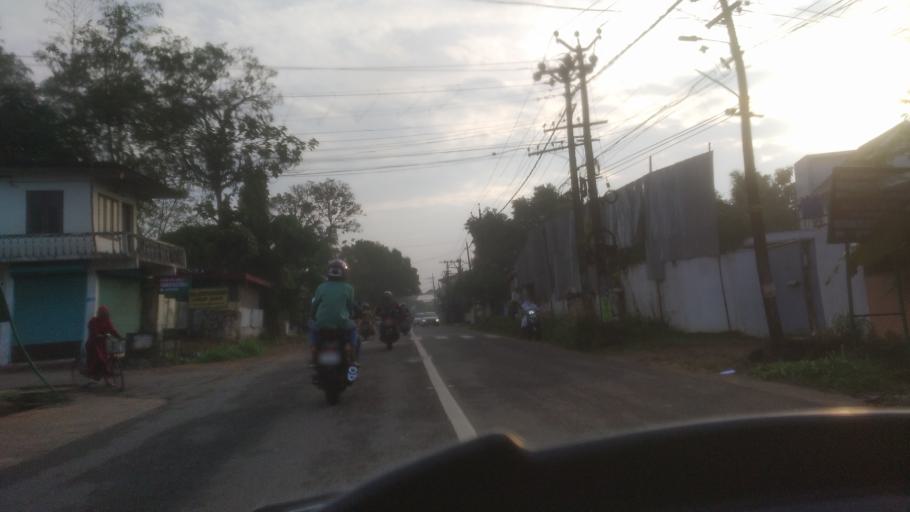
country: IN
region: Kerala
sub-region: Ernakulam
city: Perumpavur
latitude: 10.1156
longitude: 76.4527
